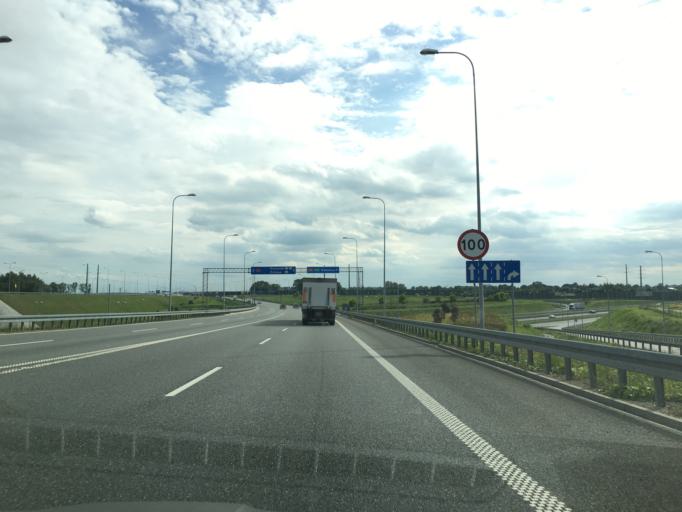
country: PL
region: Silesian Voivodeship
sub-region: Powiat gliwicki
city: Przyszowice
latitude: 50.2622
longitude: 18.7198
